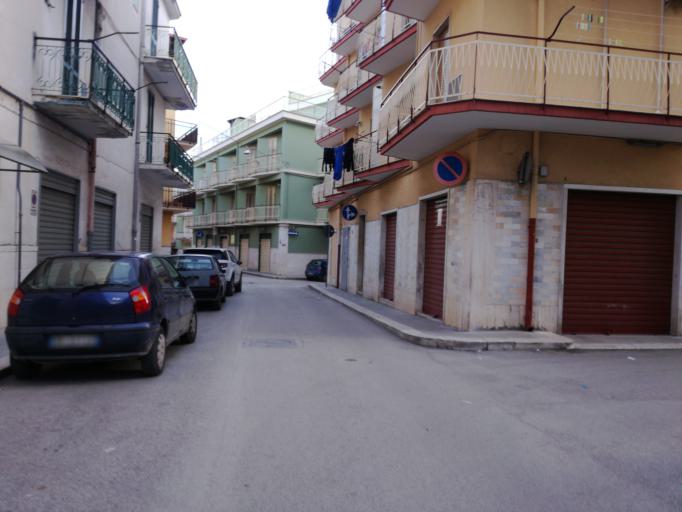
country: IT
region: Apulia
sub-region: Provincia di Bari
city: Corato
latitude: 41.1488
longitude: 16.4149
